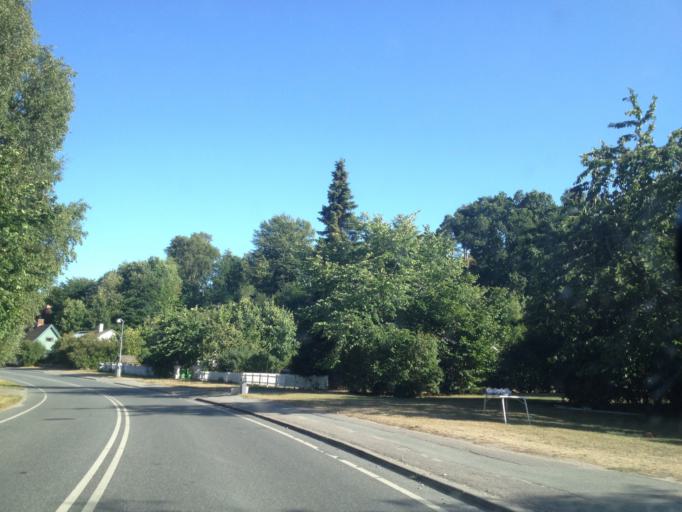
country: DK
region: Capital Region
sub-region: Gribskov Kommune
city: Helsinge
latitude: 56.0527
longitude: 12.1056
